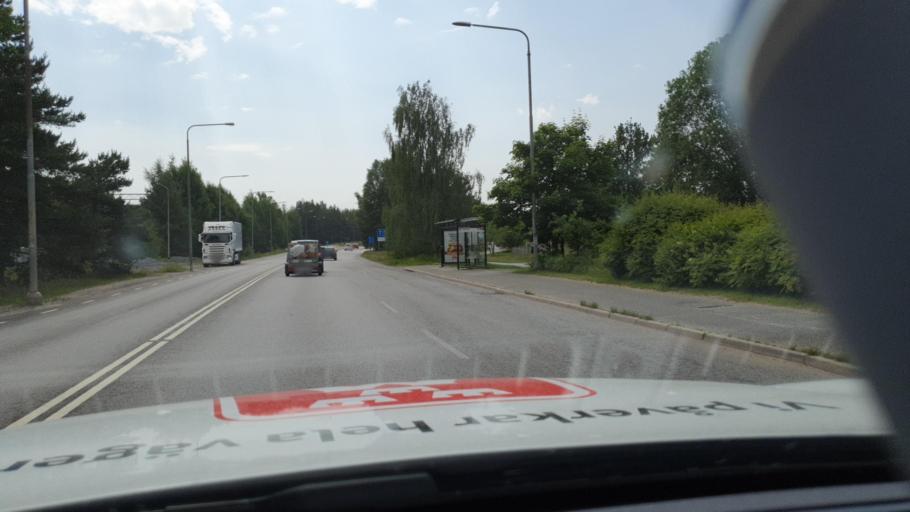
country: SE
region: Stockholm
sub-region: Haninge Kommun
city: Jordbro
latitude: 59.1408
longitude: 18.1250
